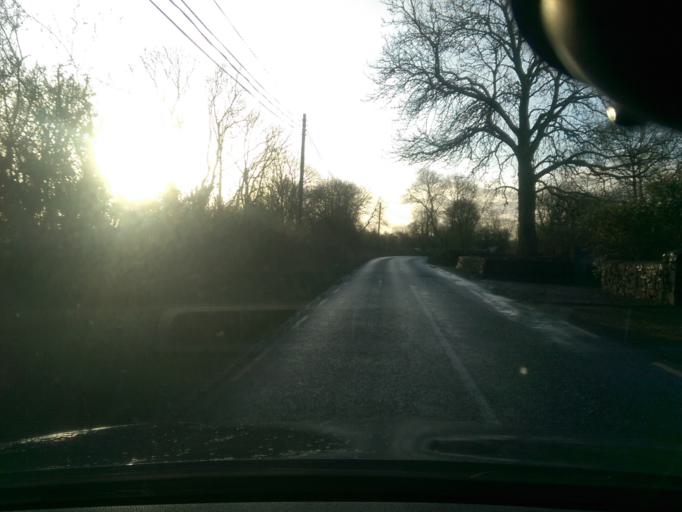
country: IE
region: Connaught
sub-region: County Galway
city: Athenry
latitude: 53.3680
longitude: -8.7004
